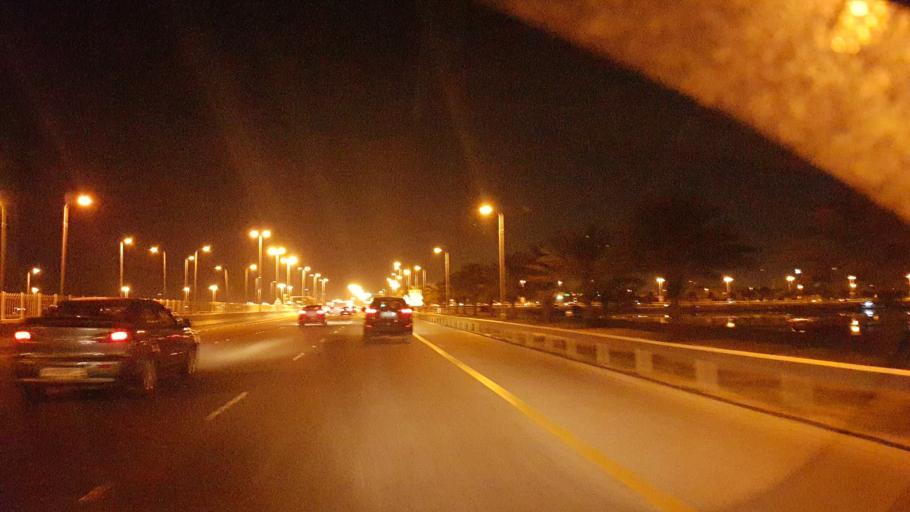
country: BH
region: Muharraq
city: Al Hadd
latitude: 26.2575
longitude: 50.6602
